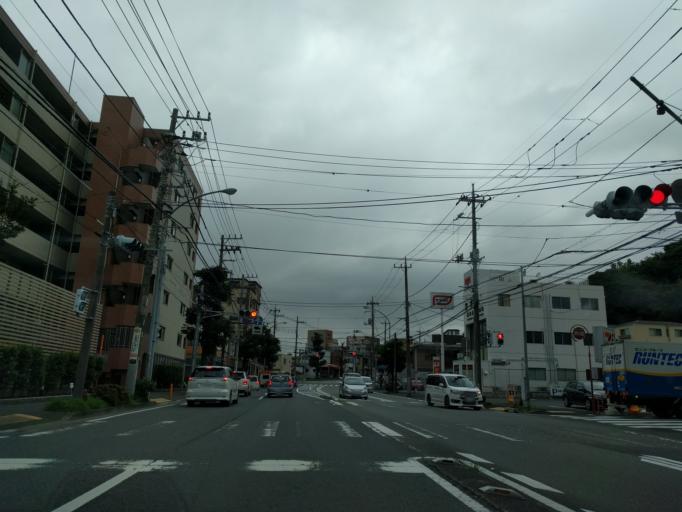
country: JP
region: Kanagawa
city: Yokohama
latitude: 35.4375
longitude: 139.5976
